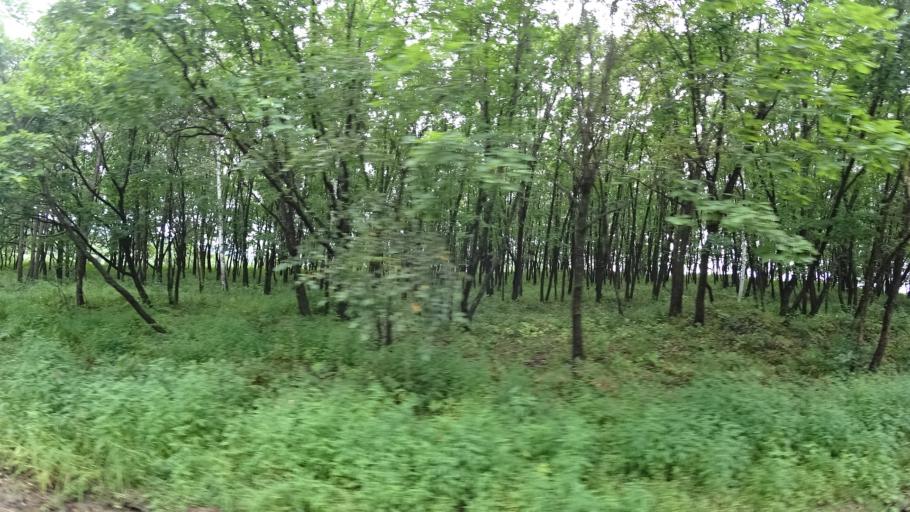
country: RU
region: Primorskiy
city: Rettikhovka
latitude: 44.0662
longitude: 132.6483
